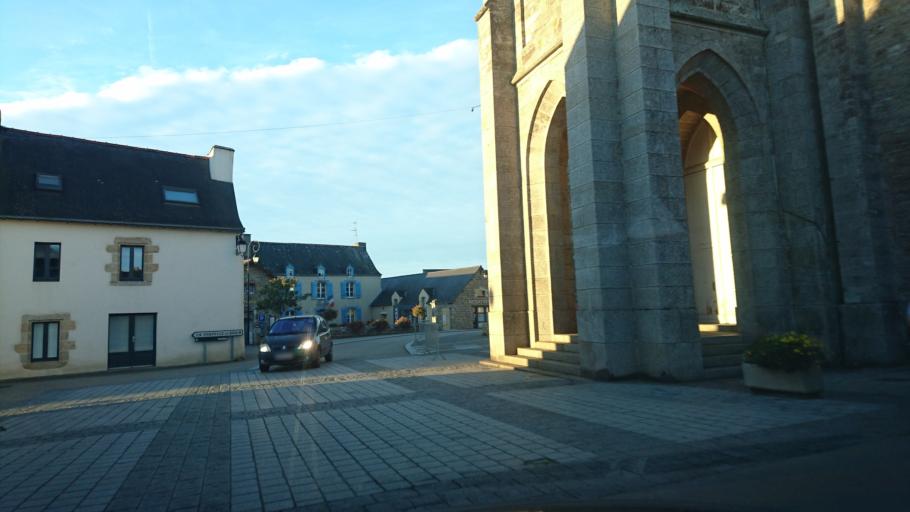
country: FR
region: Brittany
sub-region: Departement d'Ille-et-Vilaine
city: Sainte-Marie
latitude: 47.7199
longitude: -1.9753
